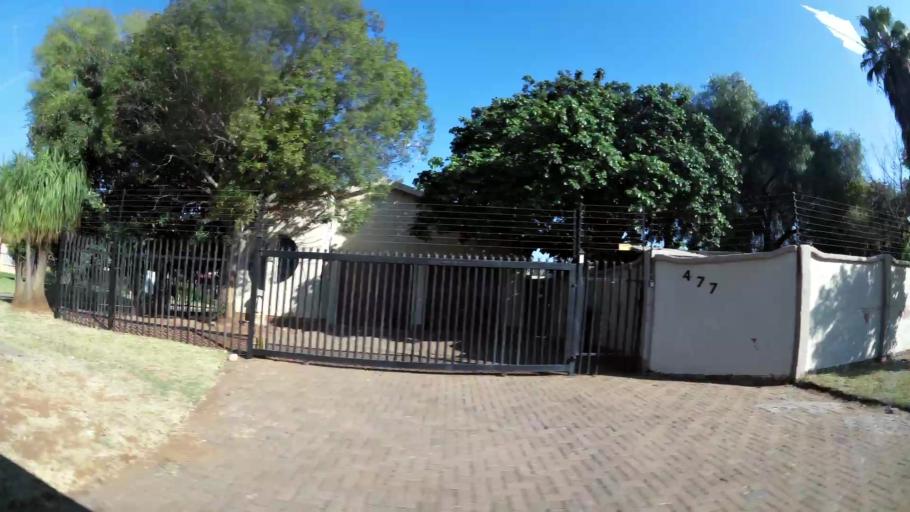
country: ZA
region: Gauteng
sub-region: City of Tshwane Metropolitan Municipality
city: Pretoria
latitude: -25.6661
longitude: 28.2343
